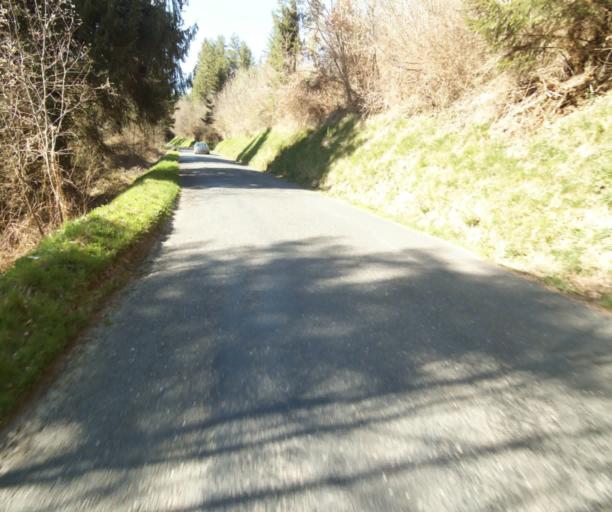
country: FR
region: Limousin
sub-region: Departement de la Correze
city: Tulle
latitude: 45.2777
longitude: 1.7345
